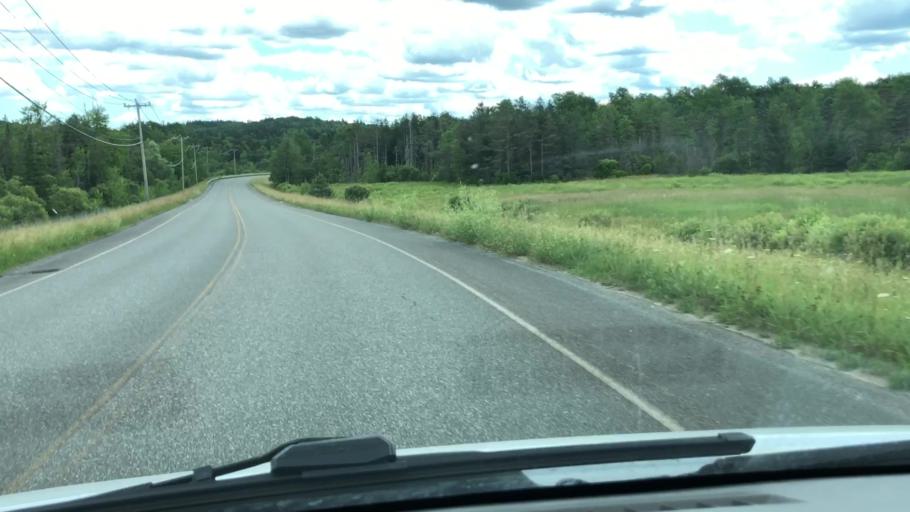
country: US
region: Massachusetts
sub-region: Berkshire County
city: Adams
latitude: 42.5336
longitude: -73.0574
